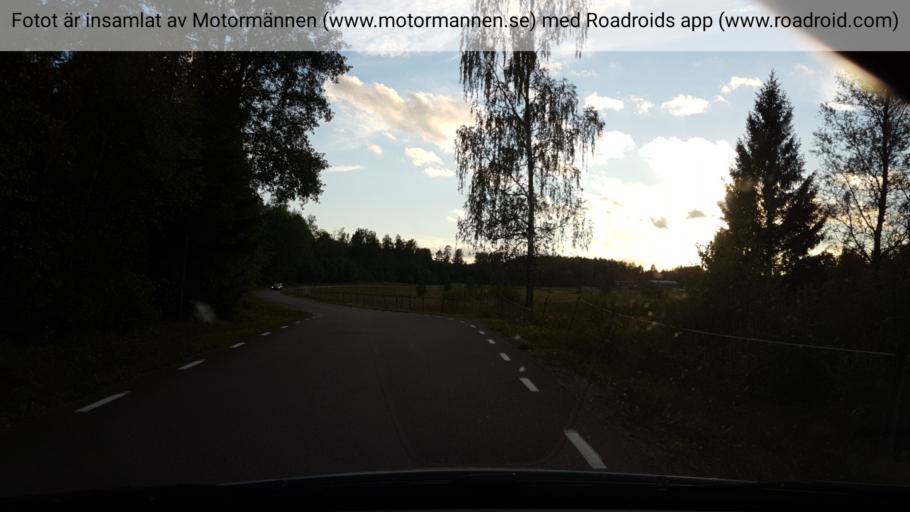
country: SE
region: Vaestmanland
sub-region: Surahammars Kommun
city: Surahammar
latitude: 59.7062
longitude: 16.1426
